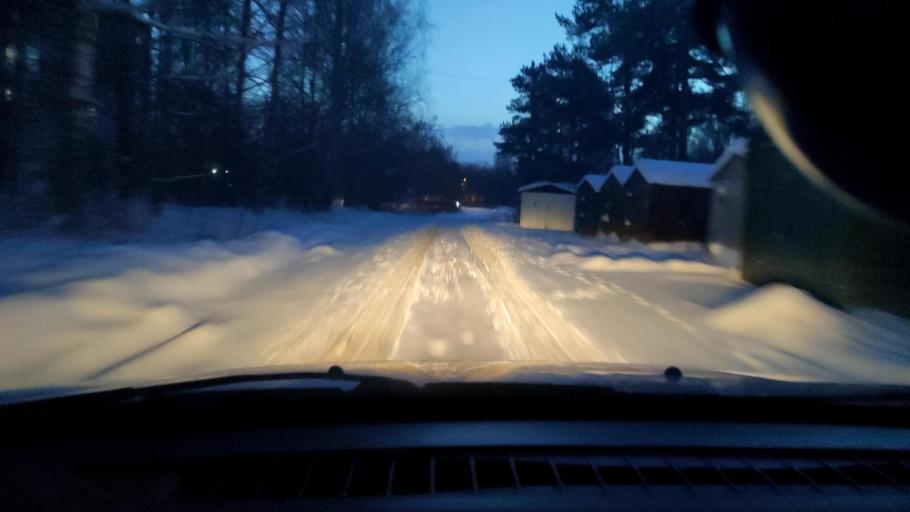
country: RU
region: Perm
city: Kondratovo
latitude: 58.0418
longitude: 56.0936
